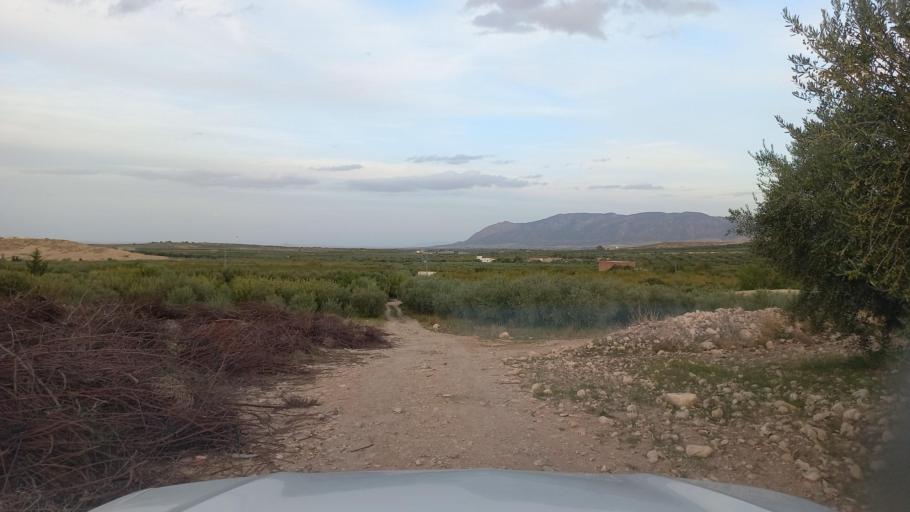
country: TN
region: Al Qasrayn
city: Sbiba
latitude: 35.4109
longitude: 9.0953
